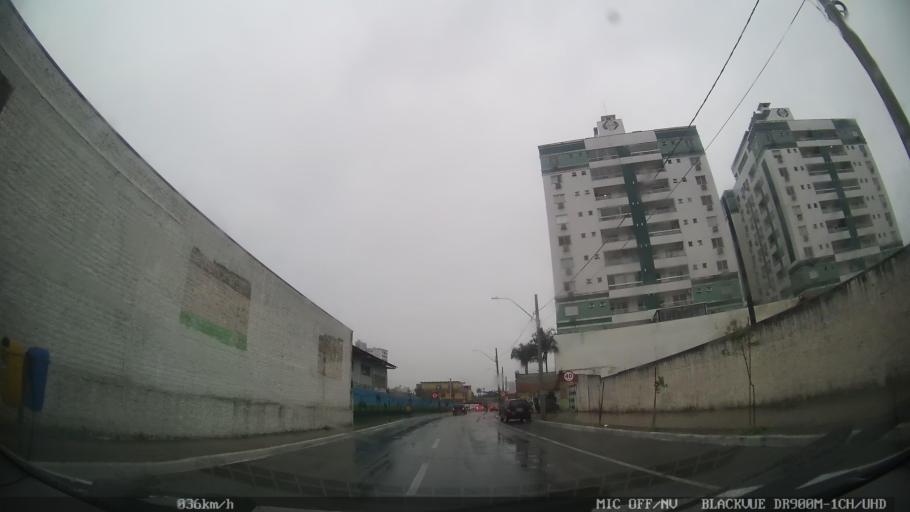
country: BR
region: Santa Catarina
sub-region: Itajai
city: Itajai
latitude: -26.9090
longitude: -48.6810
